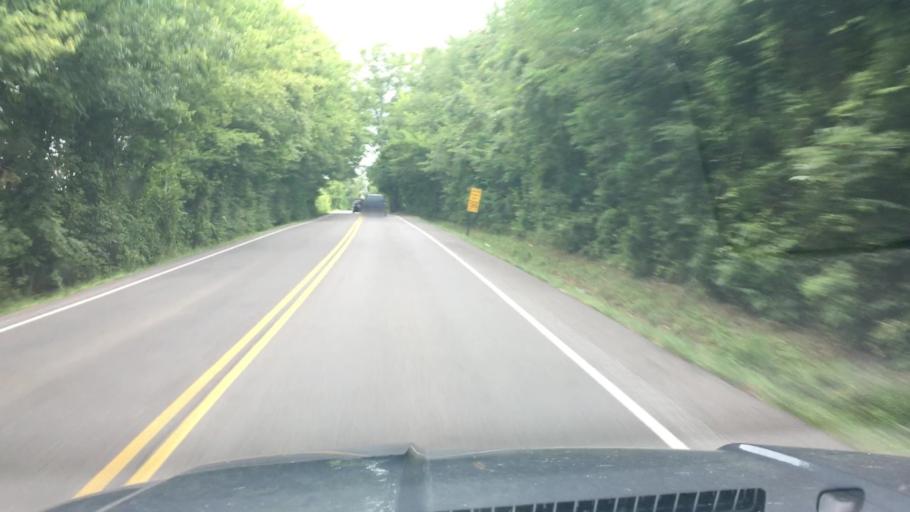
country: US
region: Tennessee
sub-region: Williamson County
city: Thompson's Station
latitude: 35.7958
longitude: -86.8638
